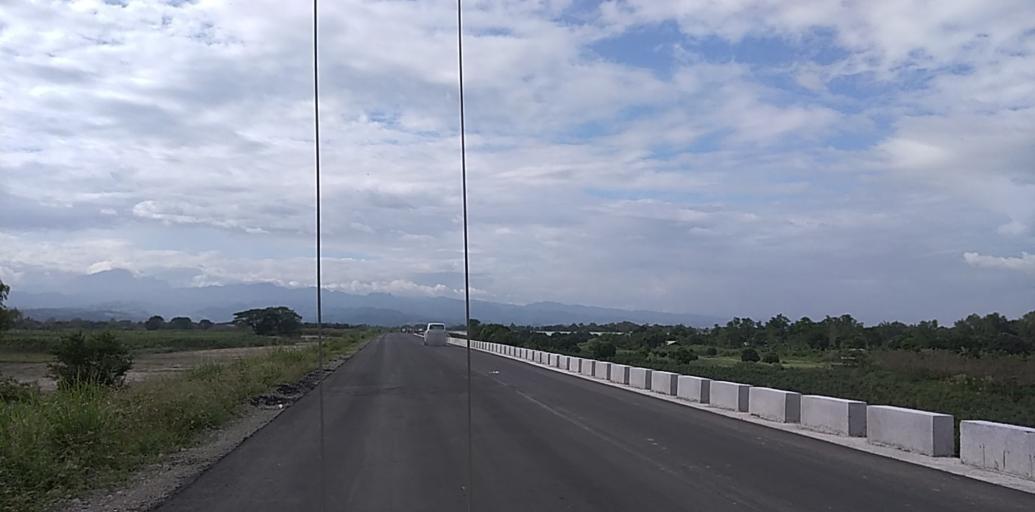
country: PH
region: Central Luzon
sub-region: Province of Pampanga
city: Pulung Santol
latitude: 15.0597
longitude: 120.5662
